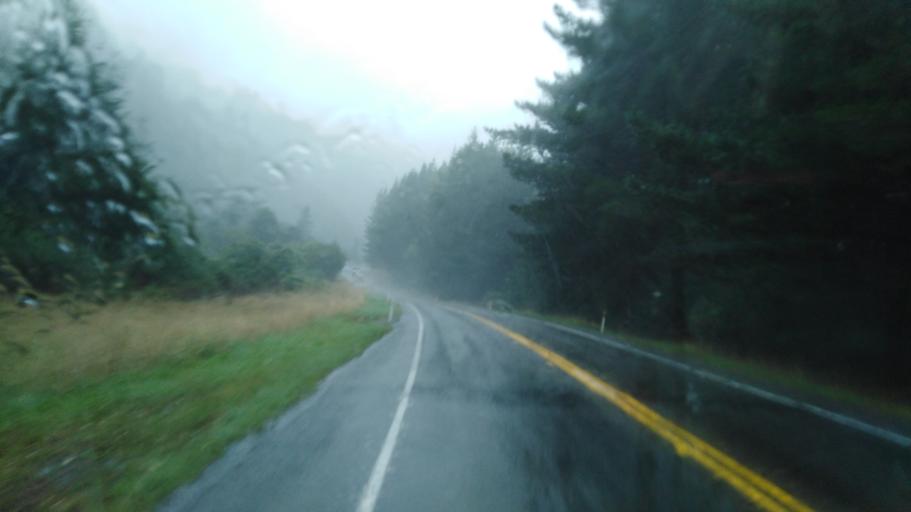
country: NZ
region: Nelson
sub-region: Nelson City
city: Nelson
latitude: -41.1912
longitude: 173.4833
